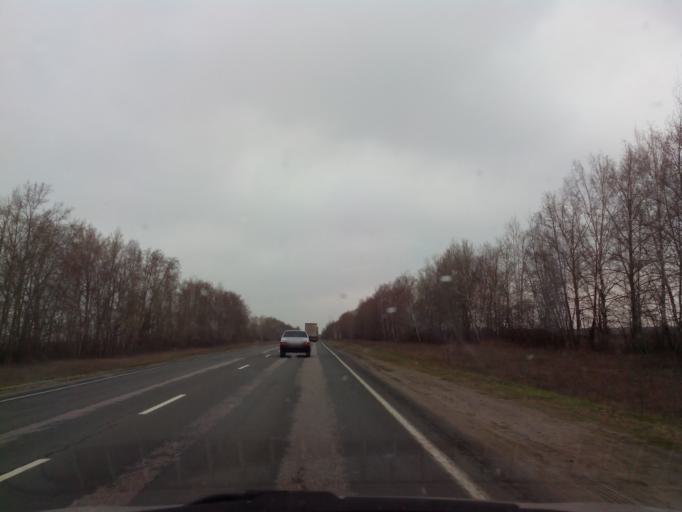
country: RU
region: Tambov
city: Pervomayskiy
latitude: 53.0992
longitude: 40.3952
